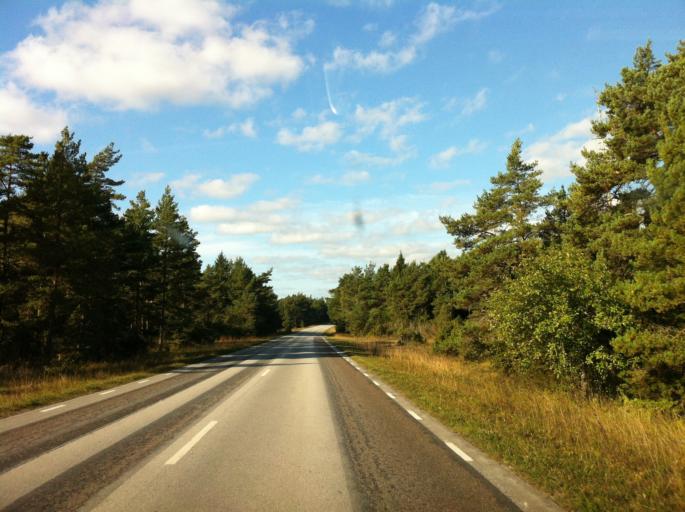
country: SE
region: Gotland
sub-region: Gotland
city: Slite
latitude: 57.4272
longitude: 18.7963
